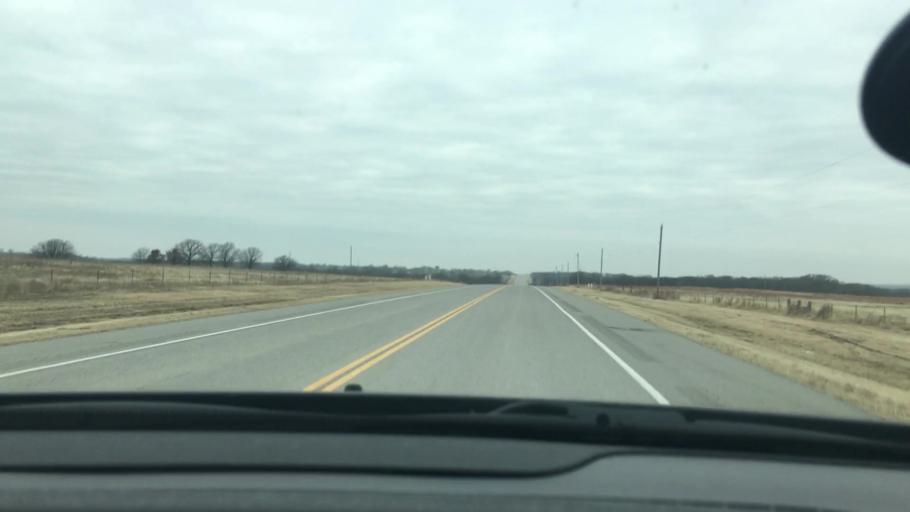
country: US
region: Oklahoma
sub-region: Murray County
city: Davis
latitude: 34.4922
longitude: -97.3928
